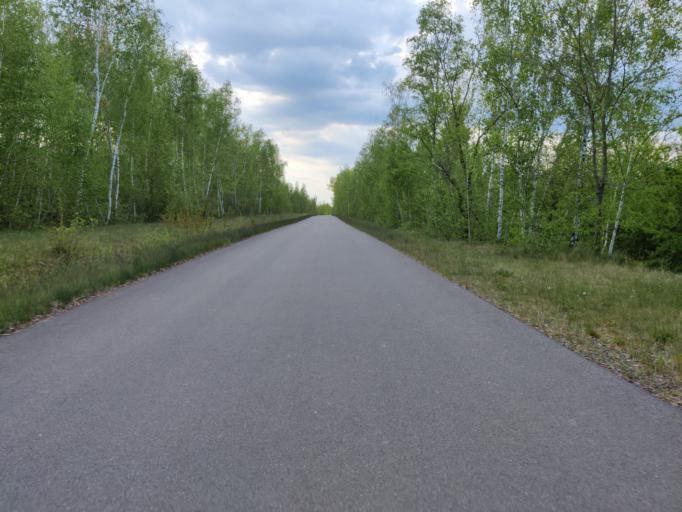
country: DE
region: Saxony
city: Espenhain
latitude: 51.2062
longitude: 12.4485
